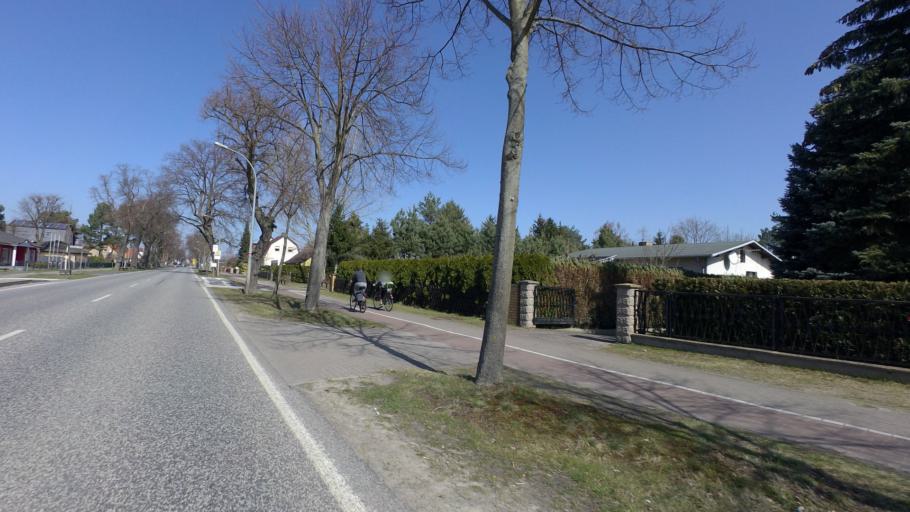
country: DE
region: Brandenburg
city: Oranienburg
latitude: 52.7296
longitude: 13.2461
